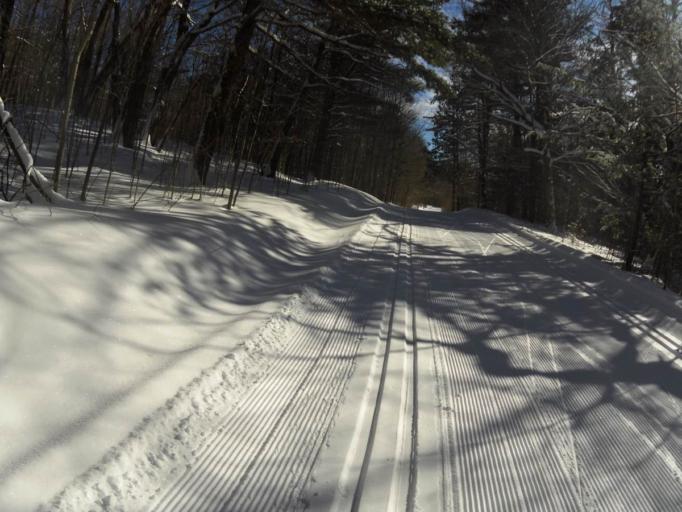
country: CA
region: Quebec
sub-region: Outaouais
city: Wakefield
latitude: 45.5887
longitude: -75.9790
